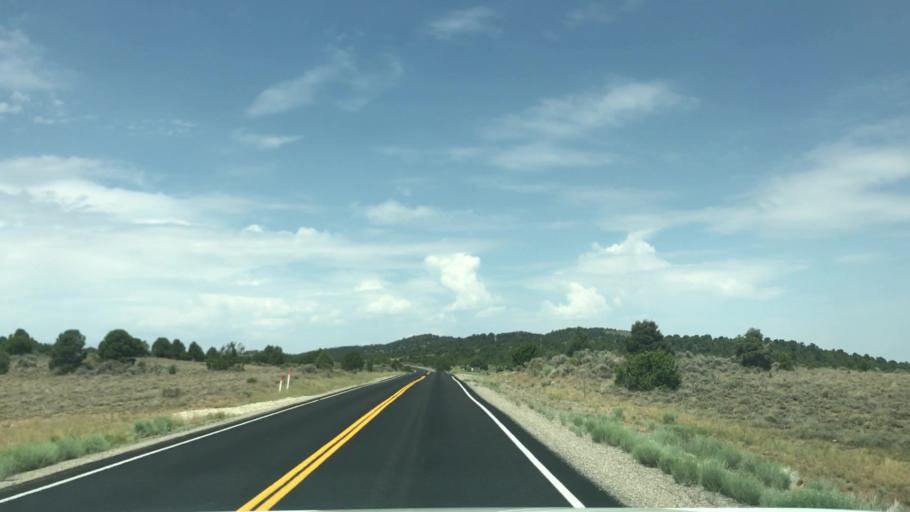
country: US
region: Nevada
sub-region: Eureka County
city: Eureka
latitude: 39.3930
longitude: -115.4582
